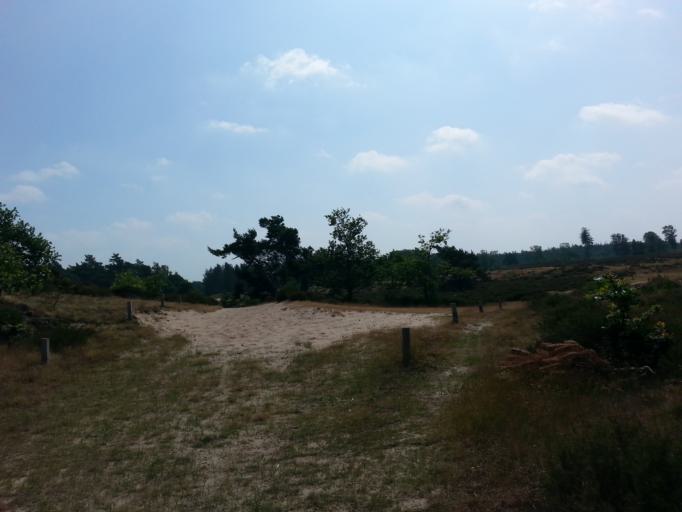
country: NL
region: Utrecht
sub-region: Gemeente Utrechtse Heuvelrug
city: Maarn
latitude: 52.0997
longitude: 5.3654
